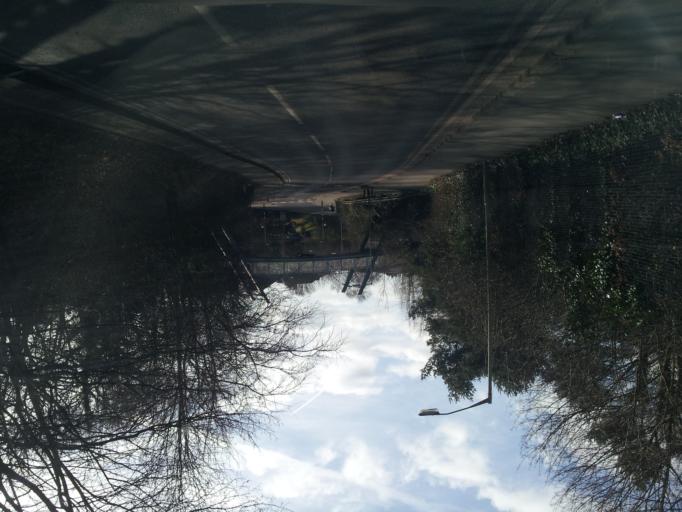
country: GB
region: England
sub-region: Hertfordshire
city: St Albans
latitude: 51.7495
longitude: -0.3205
